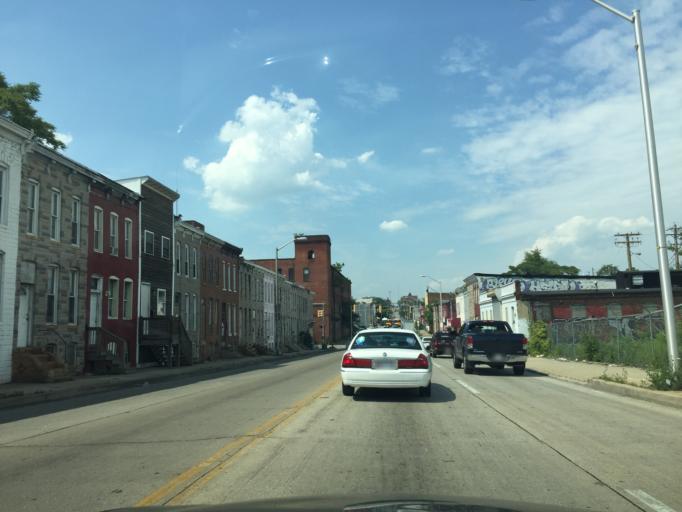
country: US
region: Maryland
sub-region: City of Baltimore
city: Baltimore
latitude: 39.2802
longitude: -76.6464
